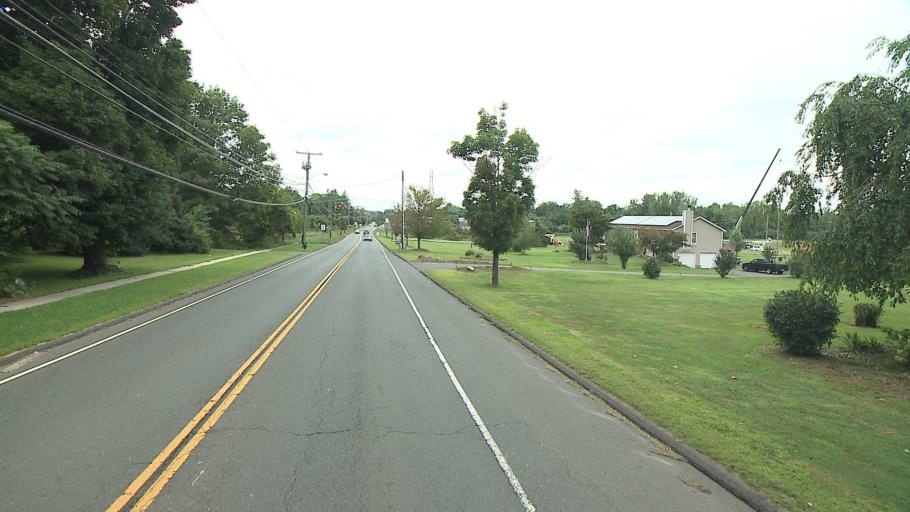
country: US
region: Connecticut
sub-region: Middlesex County
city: Middletown
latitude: 41.5721
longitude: -72.6717
